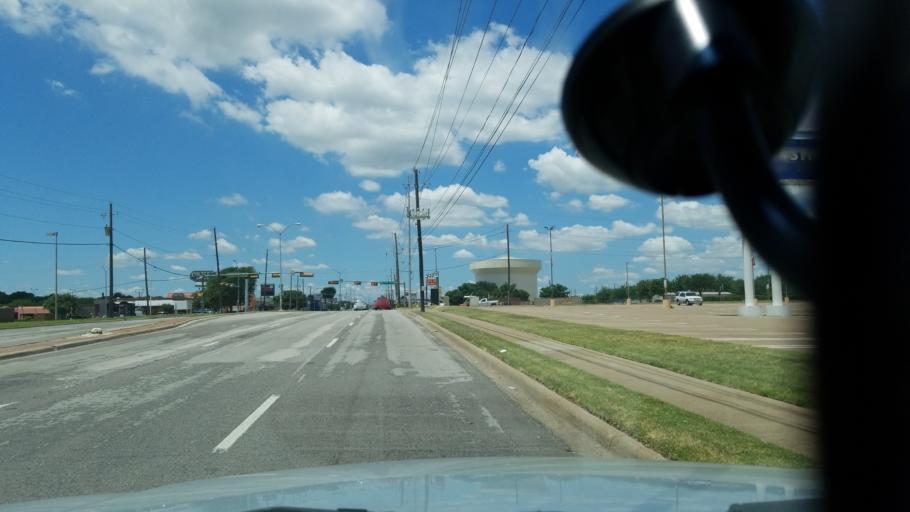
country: US
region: Texas
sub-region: Dallas County
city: Duncanville
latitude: 32.6621
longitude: -96.8803
